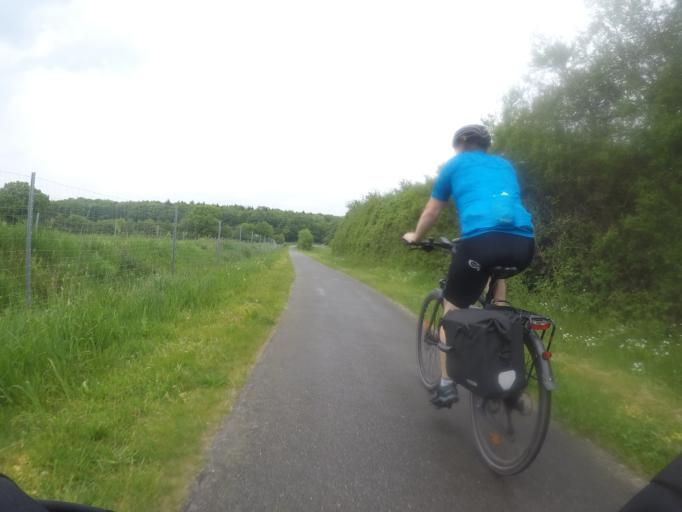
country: DE
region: Schleswig-Holstein
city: Kattendorf
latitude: 53.8543
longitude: 10.0048
